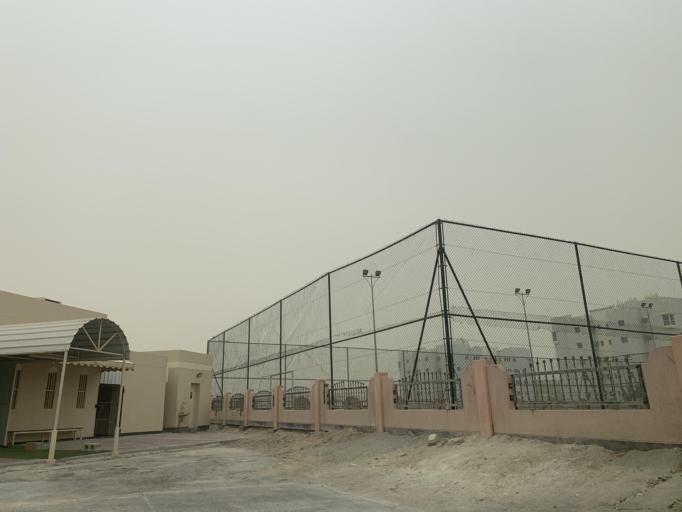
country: BH
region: Central Governorate
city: Madinat Hamad
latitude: 26.1323
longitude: 50.5235
